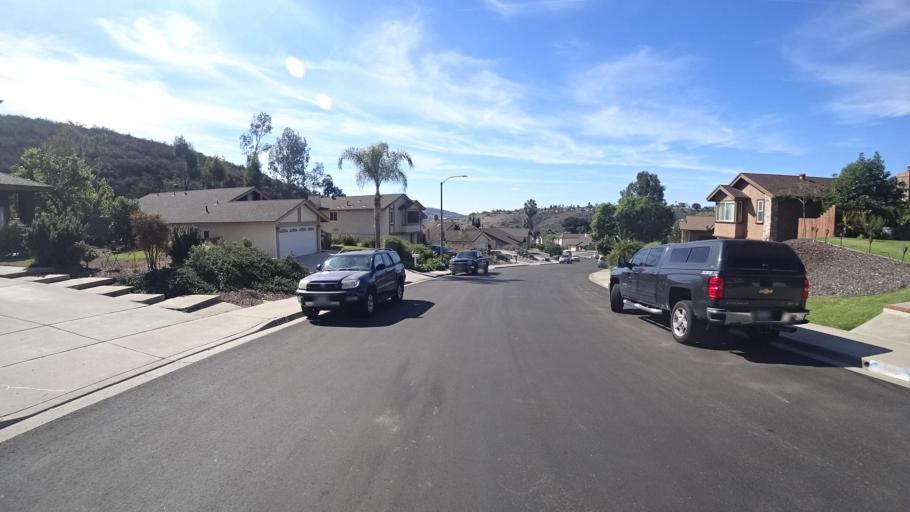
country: US
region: California
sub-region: San Diego County
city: Rancho San Diego
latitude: 32.7471
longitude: -116.9522
